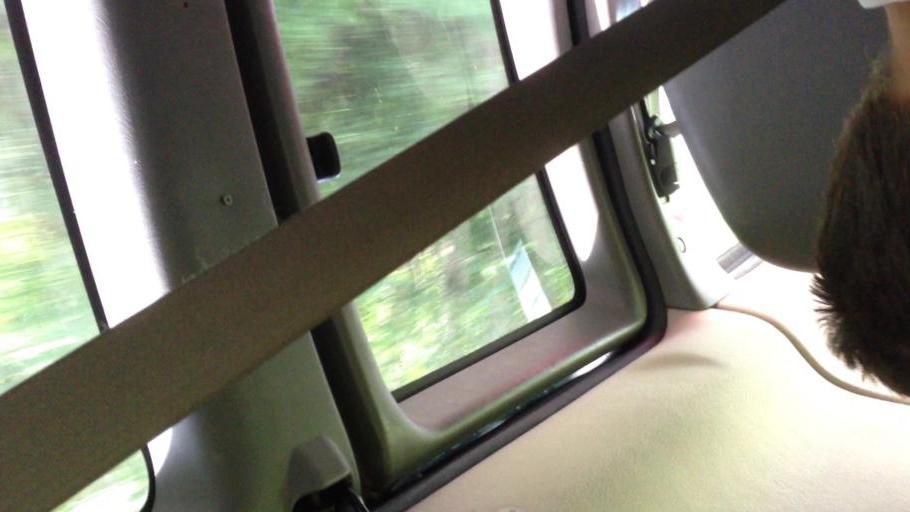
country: US
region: New York
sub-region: Dutchess County
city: Red Hook
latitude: 42.0201
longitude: -73.8973
